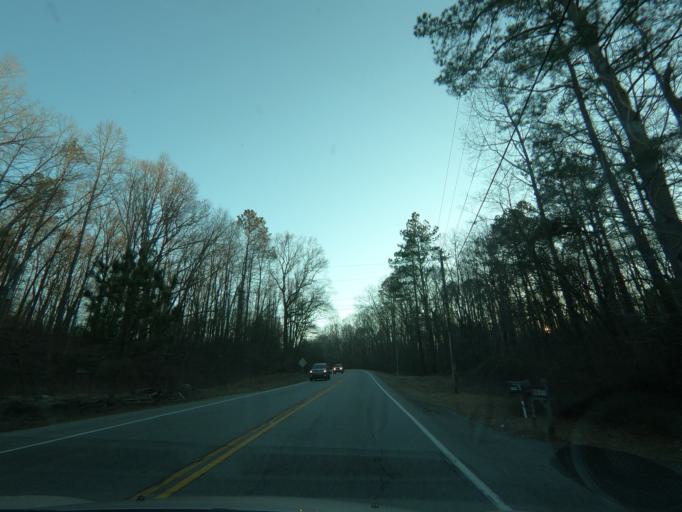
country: US
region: Georgia
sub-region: Dawson County
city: Dawsonville
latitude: 34.3445
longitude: -84.1166
